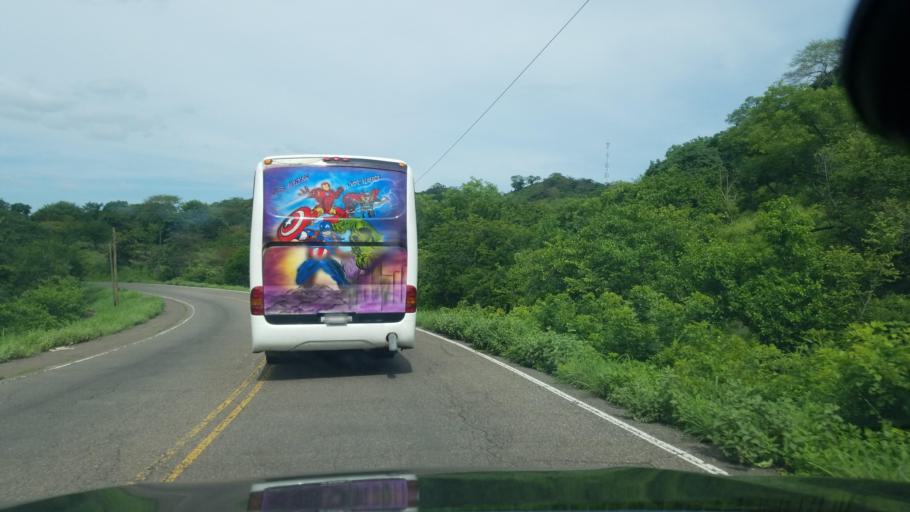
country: HN
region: Choluteca
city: Santa Ana de Yusguare
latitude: 13.3738
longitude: -87.0728
